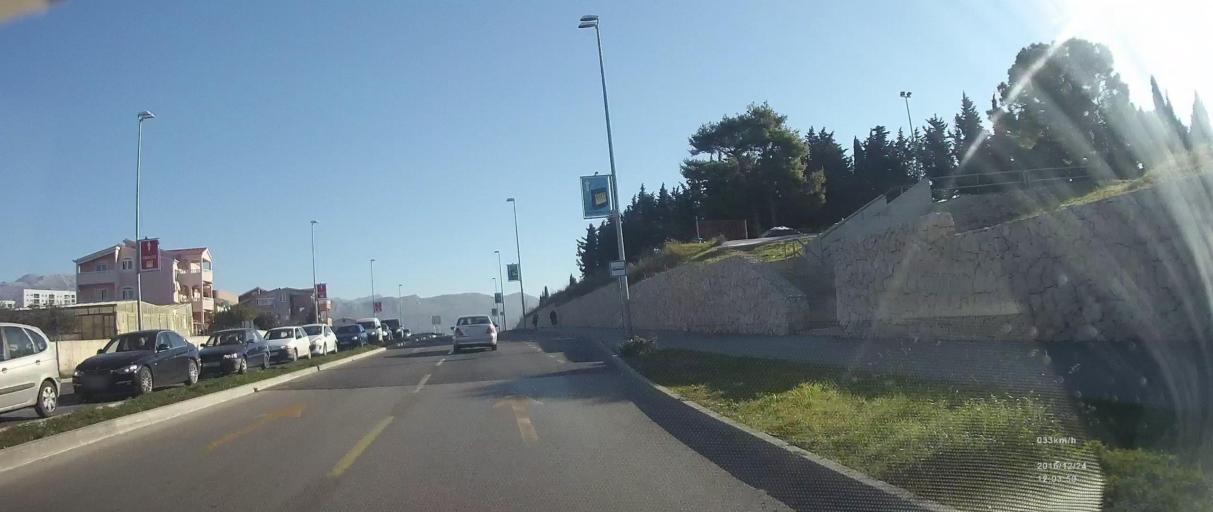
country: HR
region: Splitsko-Dalmatinska
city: Kamen
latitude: 43.5150
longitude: 16.4930
